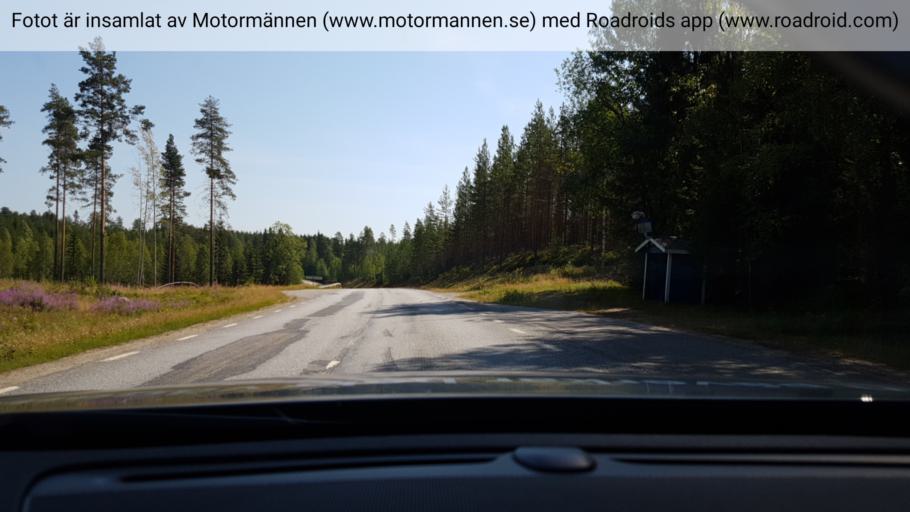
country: SE
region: Vaesterbotten
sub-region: Vindelns Kommun
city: Vindeln
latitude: 64.2441
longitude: 19.6593
